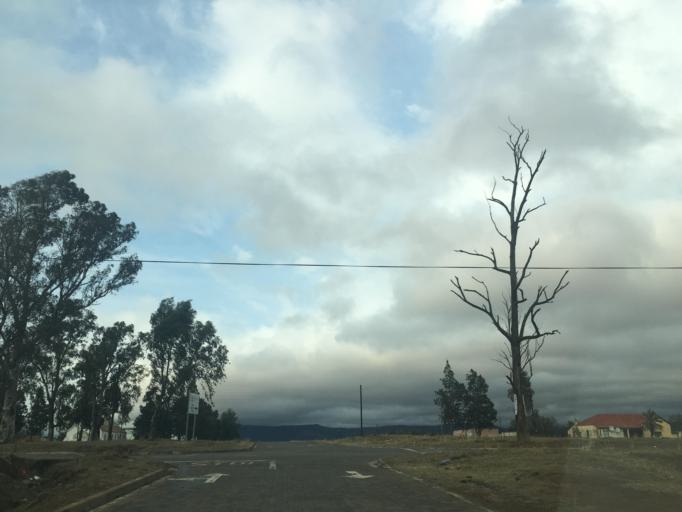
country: ZA
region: Eastern Cape
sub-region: Chris Hani District Municipality
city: Cala
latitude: -31.5262
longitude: 27.6998
